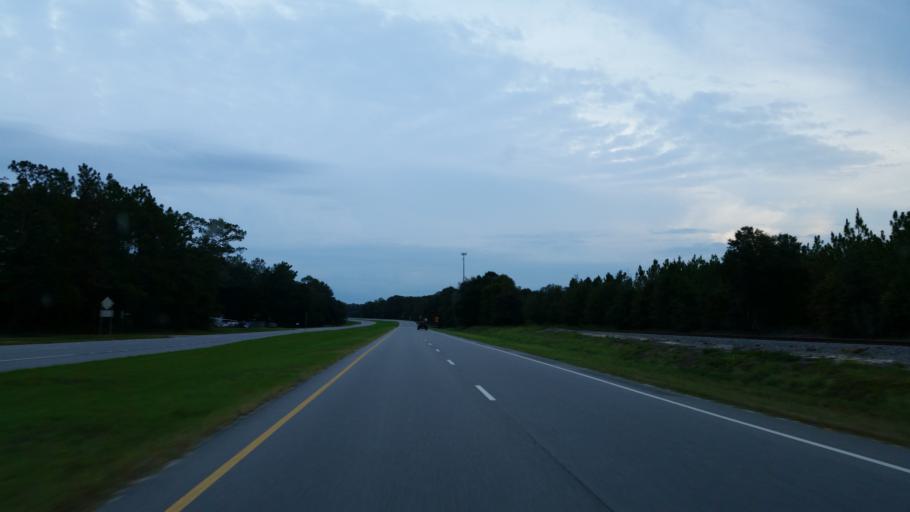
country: US
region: Georgia
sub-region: Lowndes County
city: Valdosta
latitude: 30.6972
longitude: -83.2105
